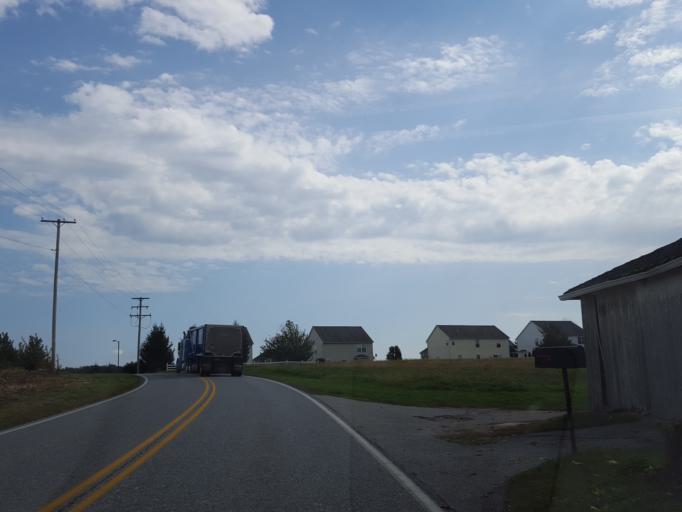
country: US
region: Pennsylvania
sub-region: York County
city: Yoe
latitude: 39.9125
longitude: -76.6536
